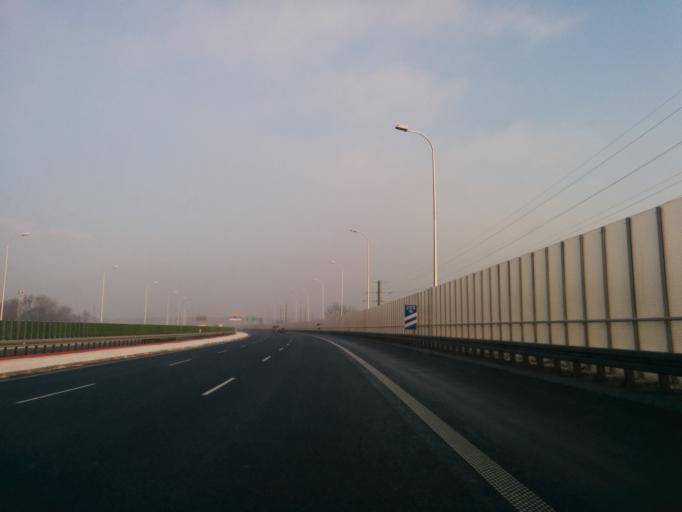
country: PL
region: Silesian Voivodeship
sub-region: Gliwice
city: Gliwice
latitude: 50.3040
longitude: 18.7286
